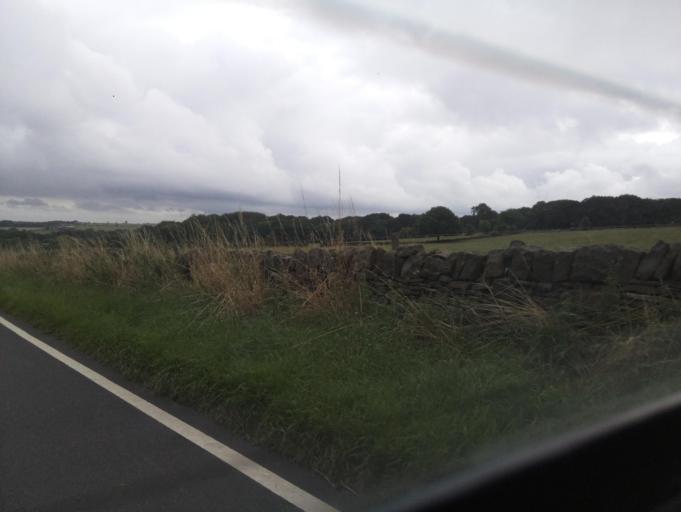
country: GB
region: England
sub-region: Kirklees
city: Shelley
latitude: 53.5814
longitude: -1.6914
